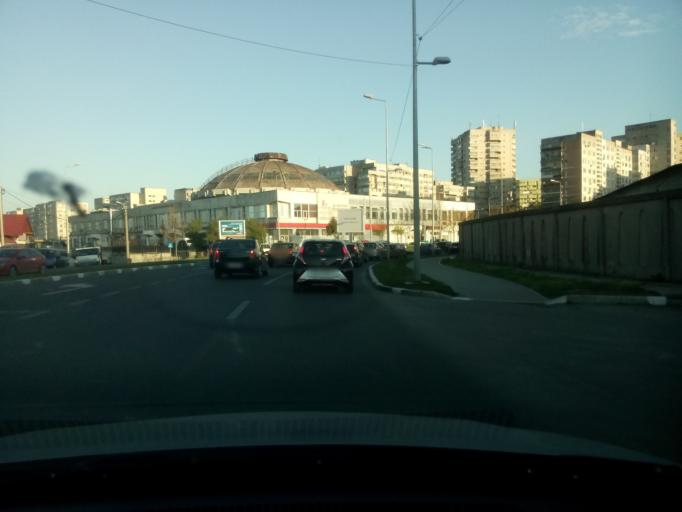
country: RO
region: Ilfov
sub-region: Comuna Fundeni-Dobroesti
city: Fundeni
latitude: 44.4458
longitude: 26.1563
